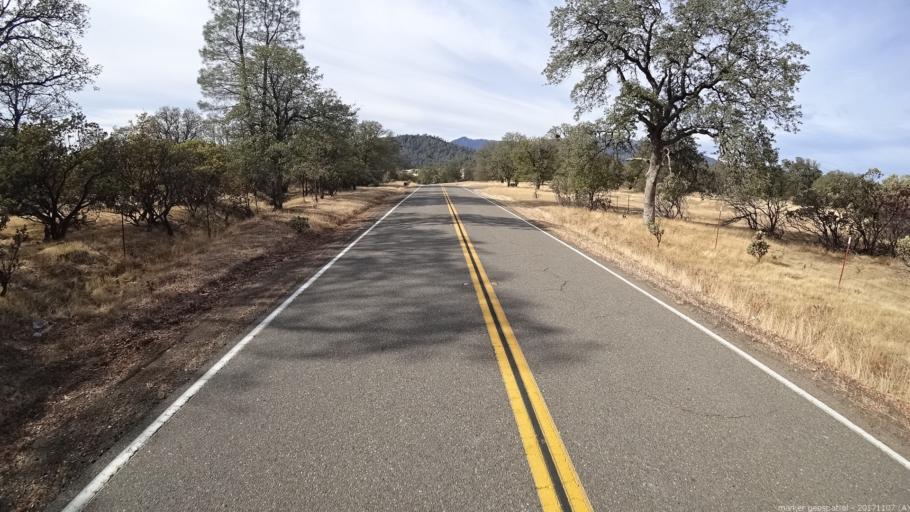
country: US
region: California
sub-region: Shasta County
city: Shasta
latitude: 40.5064
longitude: -122.5363
